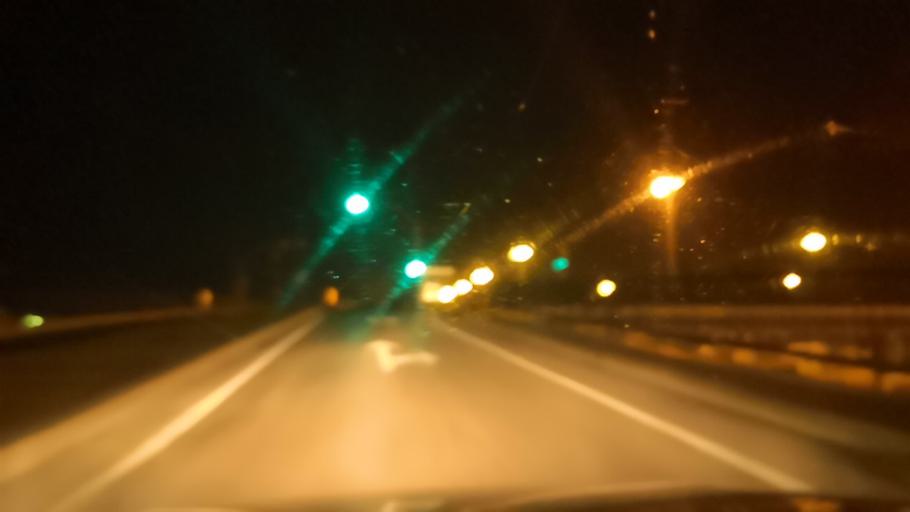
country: PT
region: Setubal
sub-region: Setubal
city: Setubal
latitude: 38.5146
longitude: -8.8652
